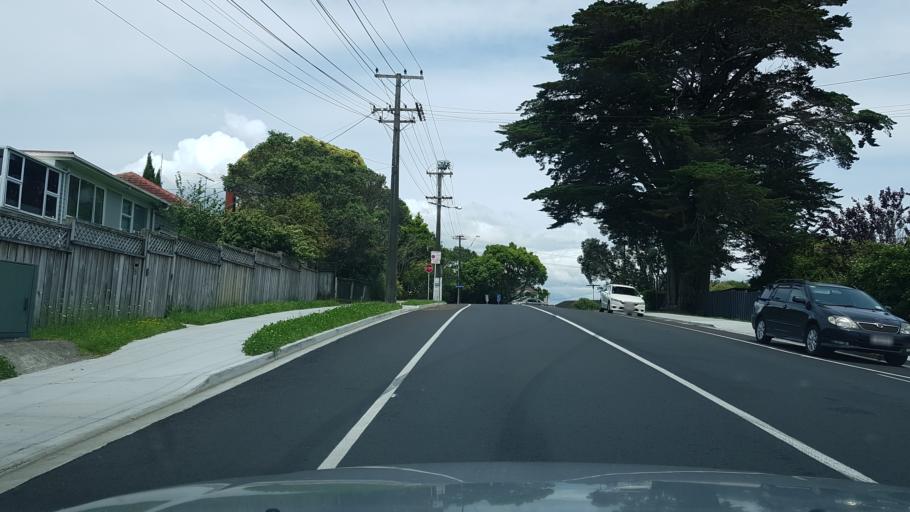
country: NZ
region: Auckland
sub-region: Auckland
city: North Shore
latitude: -36.8025
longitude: 174.7462
